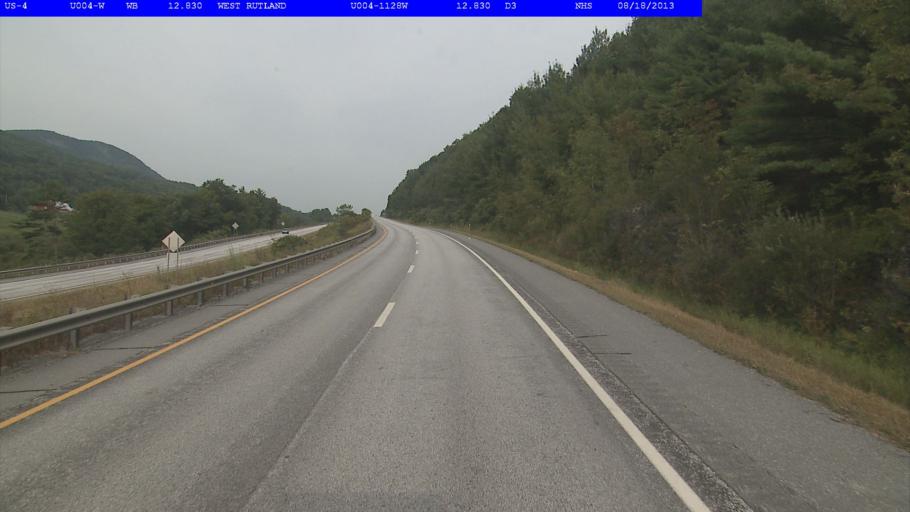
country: US
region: Vermont
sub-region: Rutland County
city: West Rutland
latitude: 43.6063
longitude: -73.0687
